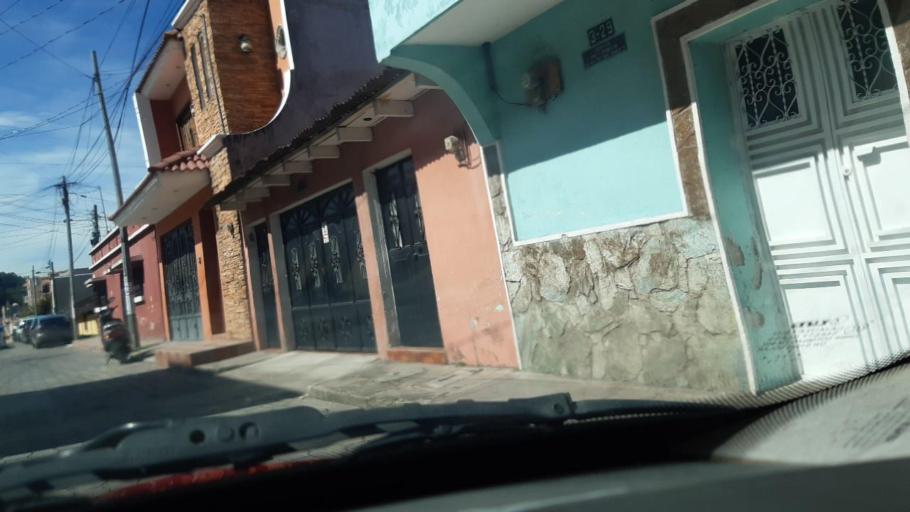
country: GT
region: Quetzaltenango
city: Salcaja
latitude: 14.8809
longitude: -91.4544
